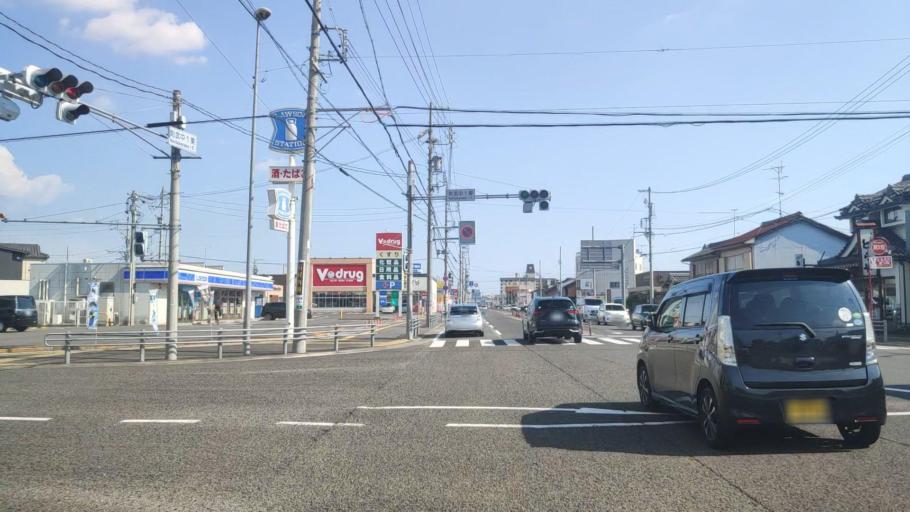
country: JP
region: Gifu
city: Gifu-shi
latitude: 35.4410
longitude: 136.7468
